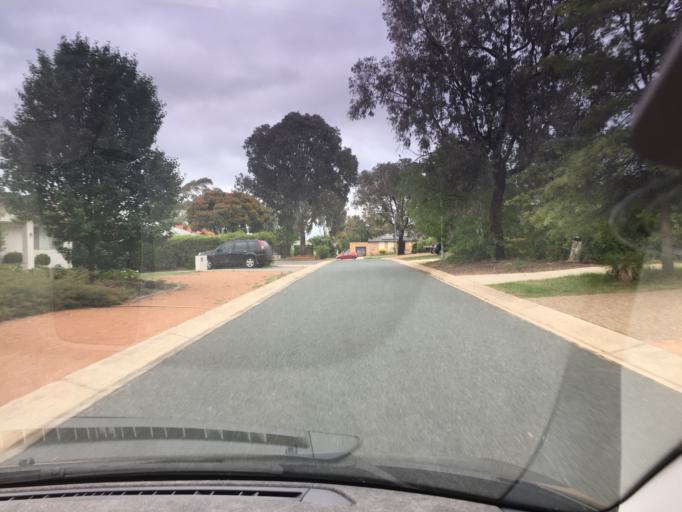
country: AU
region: Australian Capital Territory
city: Kaleen
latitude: -35.2183
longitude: 149.1121
